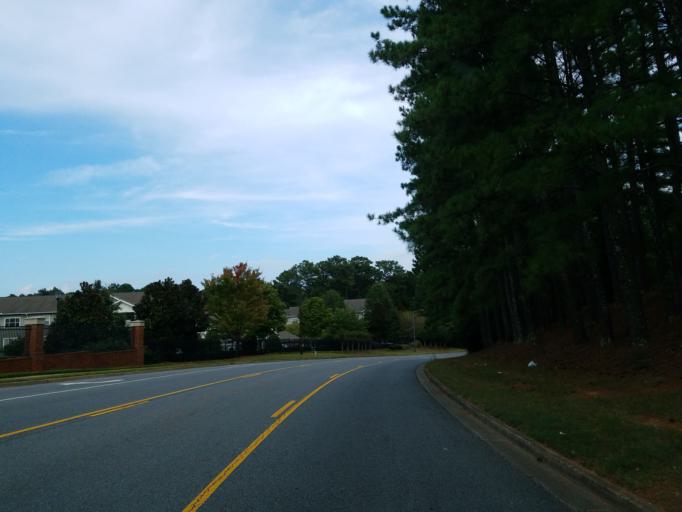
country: US
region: Georgia
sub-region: Cobb County
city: Marietta
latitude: 33.9942
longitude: -84.5444
